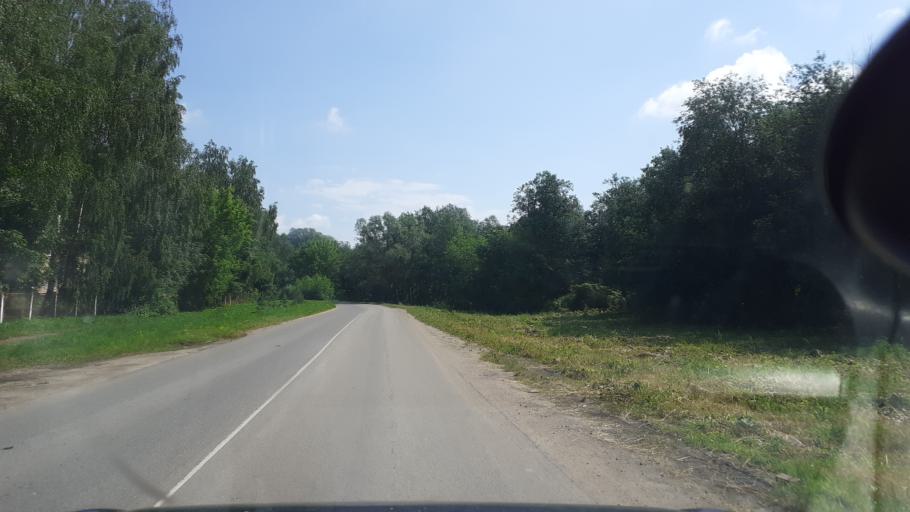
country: RU
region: Moskovskaya
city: Ateptsevo
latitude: 55.3210
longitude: 36.7521
